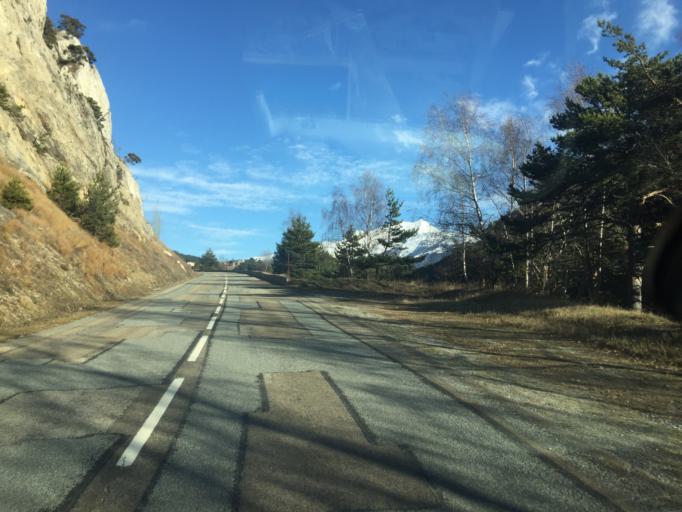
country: FR
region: Rhone-Alpes
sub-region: Departement de la Savoie
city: Modane
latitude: 45.2227
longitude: 6.7270
